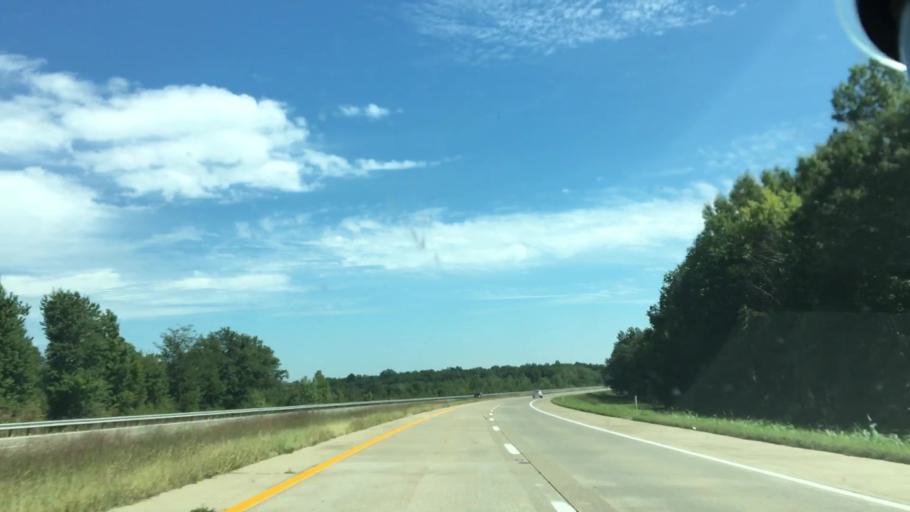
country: US
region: Kentucky
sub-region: Daviess County
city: Owensboro
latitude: 37.7632
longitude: -87.3095
